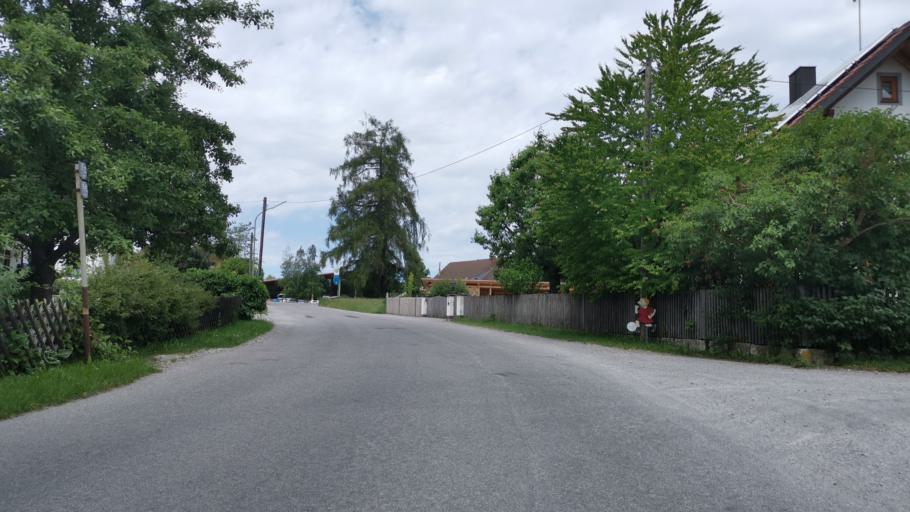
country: DE
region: Bavaria
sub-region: Upper Bavaria
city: Hattenhofen
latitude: 48.2215
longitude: 11.0984
